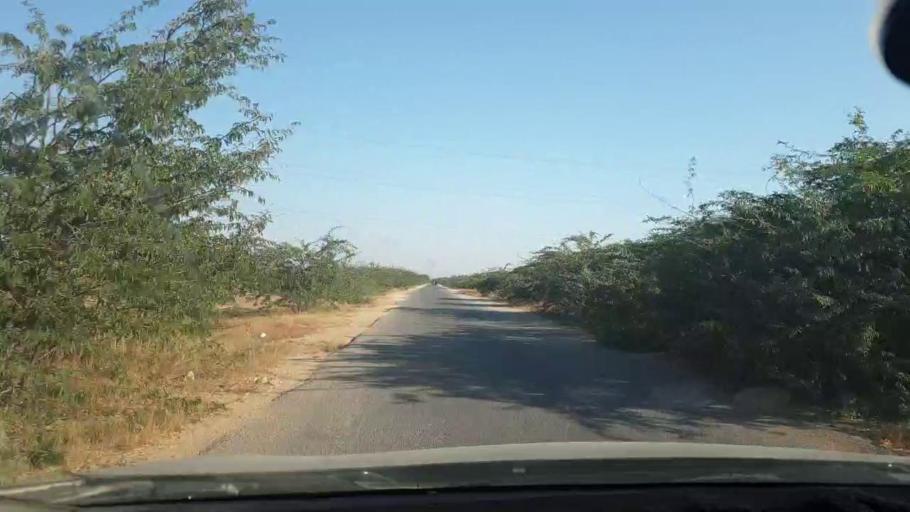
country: PK
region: Sindh
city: Malir Cantonment
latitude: 25.1604
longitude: 67.1941
